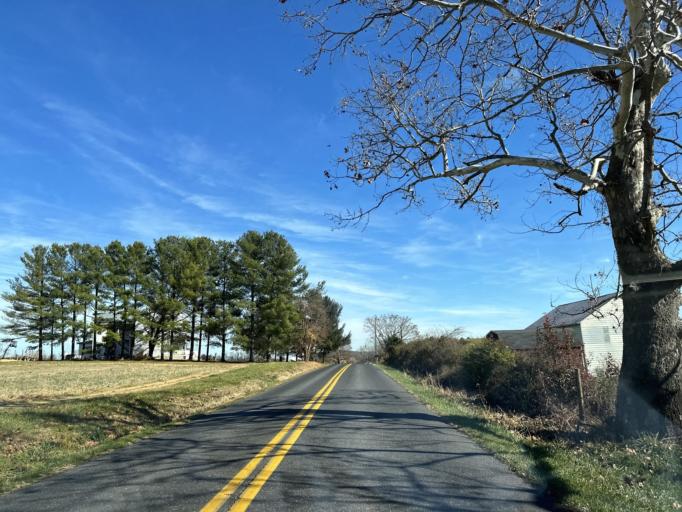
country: US
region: Virginia
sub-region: Augusta County
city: Fishersville
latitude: 38.1193
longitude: -78.9526
